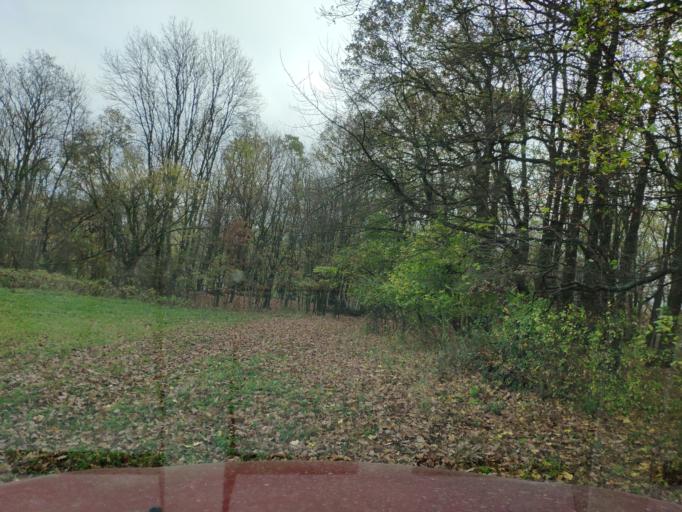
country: SK
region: Presovsky
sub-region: Okres Presov
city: Presov
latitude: 49.0034
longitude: 21.2015
